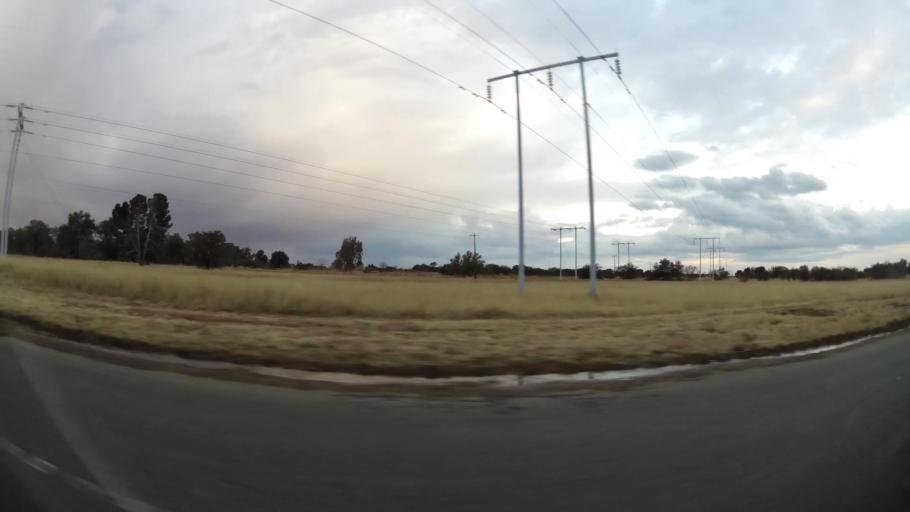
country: ZA
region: Orange Free State
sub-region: Lejweleputswa District Municipality
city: Welkom
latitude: -27.9632
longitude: 26.7604
